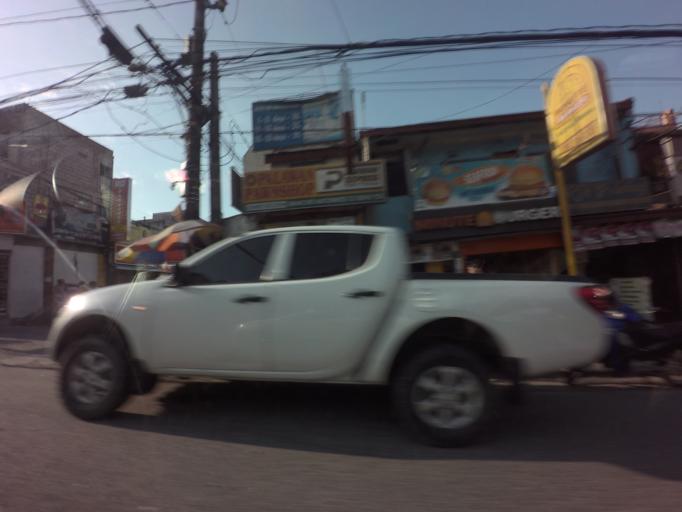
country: PH
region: Calabarzon
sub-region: Province of Rizal
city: Taguig
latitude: 14.4887
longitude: 121.0597
